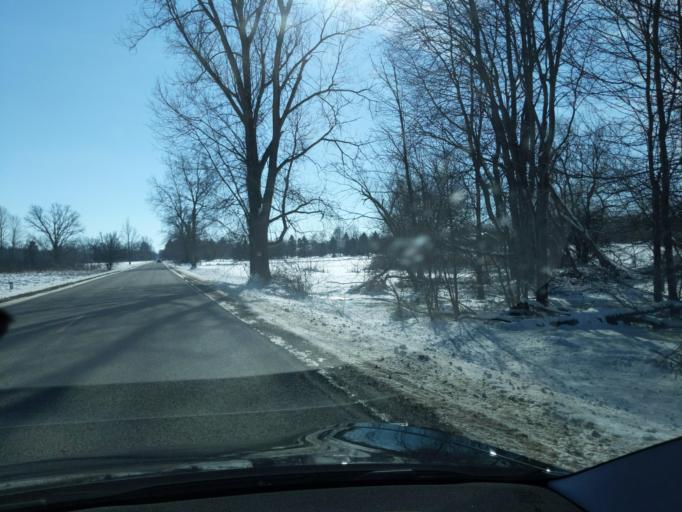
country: US
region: Michigan
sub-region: Livingston County
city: Fowlerville
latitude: 42.5948
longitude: -84.0748
